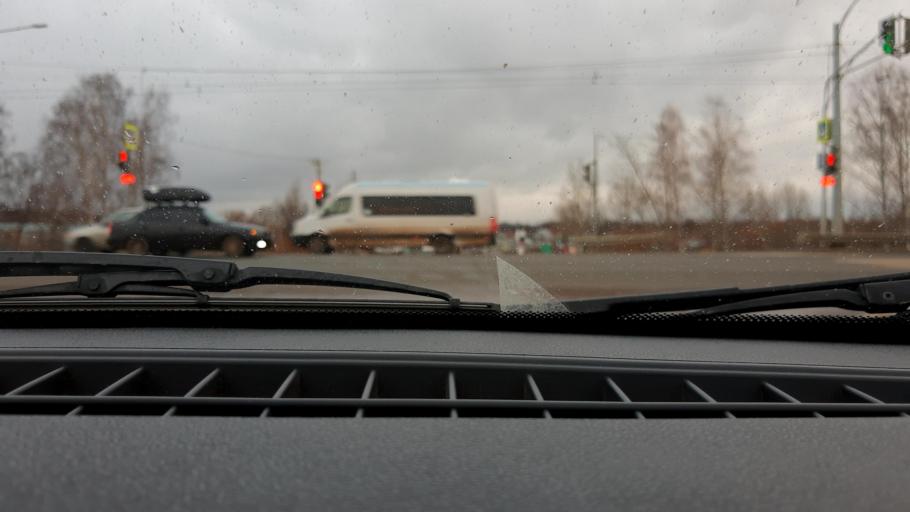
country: RU
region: Bashkortostan
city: Mikhaylovka
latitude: 54.7696
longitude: 55.9116
